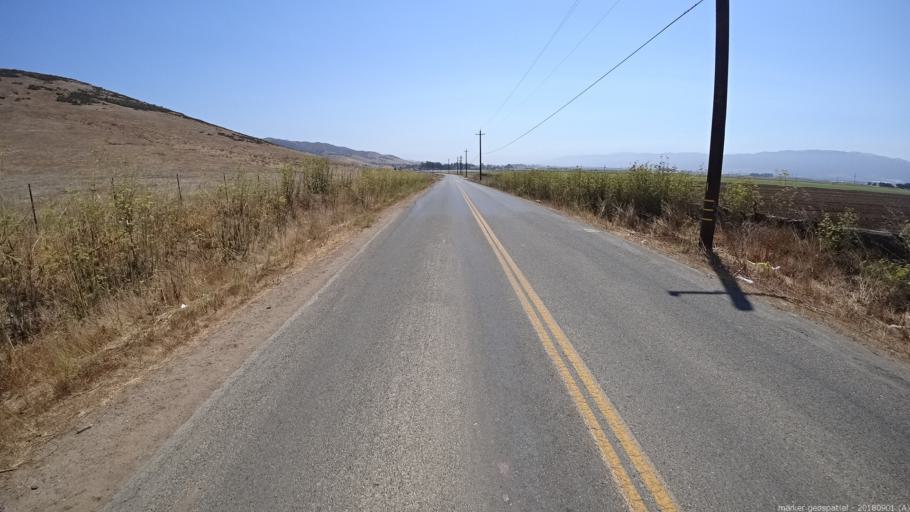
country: US
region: California
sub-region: Monterey County
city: Salinas
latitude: 36.6869
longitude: -121.5644
